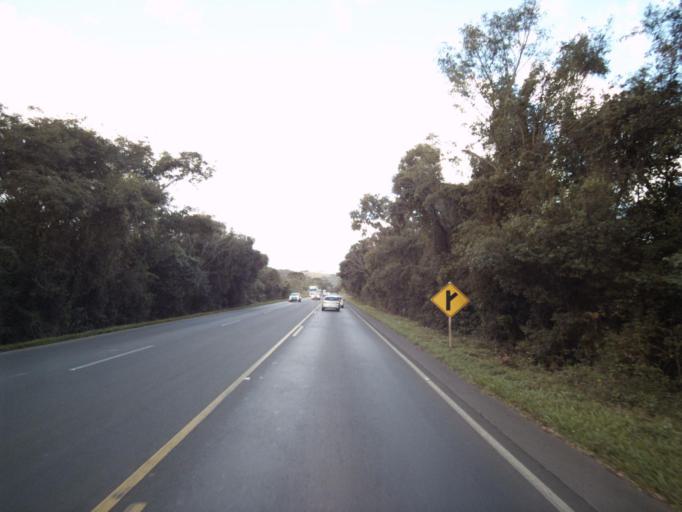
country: BR
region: Santa Catarina
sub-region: Joacaba
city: Joacaba
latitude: -27.3066
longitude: -51.3788
